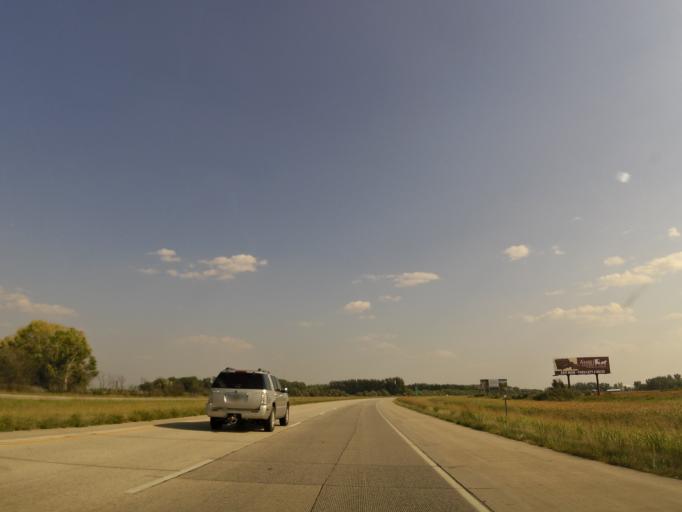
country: US
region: North Dakota
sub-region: Grand Forks County
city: Grand Forks
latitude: 48.0014
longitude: -97.1001
